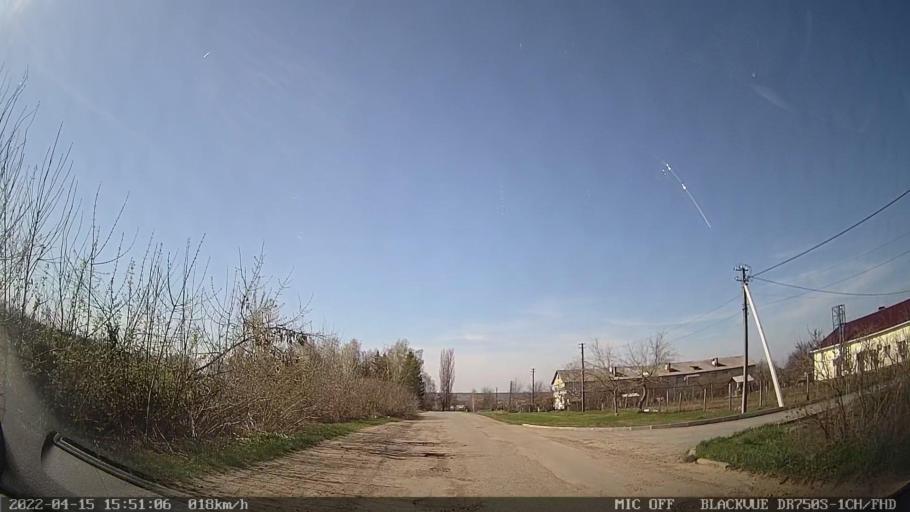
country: MD
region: Raionul Ocnita
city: Otaci
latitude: 48.3933
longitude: 27.8994
